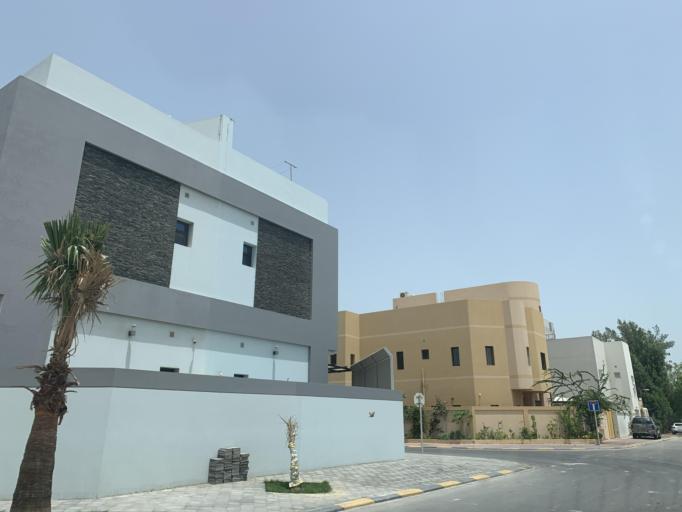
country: BH
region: Northern
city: Sitrah
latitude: 26.1441
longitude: 50.5888
